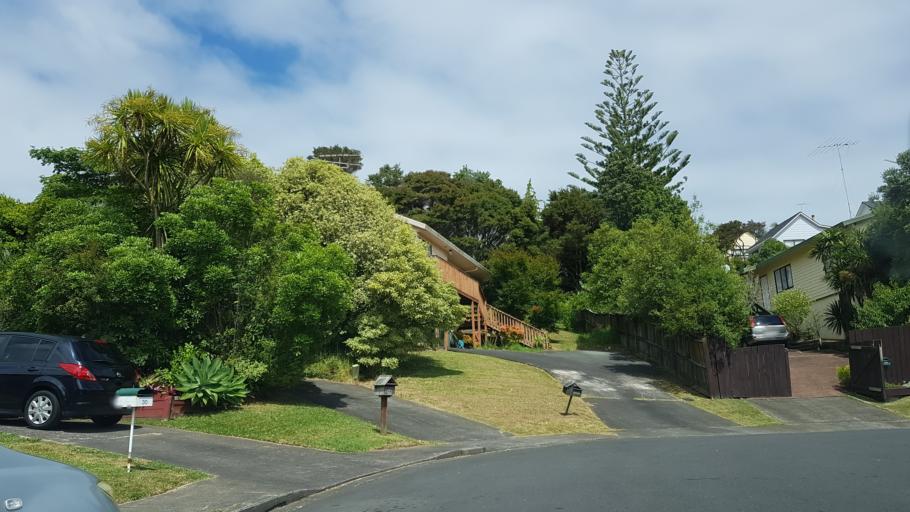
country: NZ
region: Auckland
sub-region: Auckland
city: North Shore
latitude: -36.7777
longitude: 174.7077
